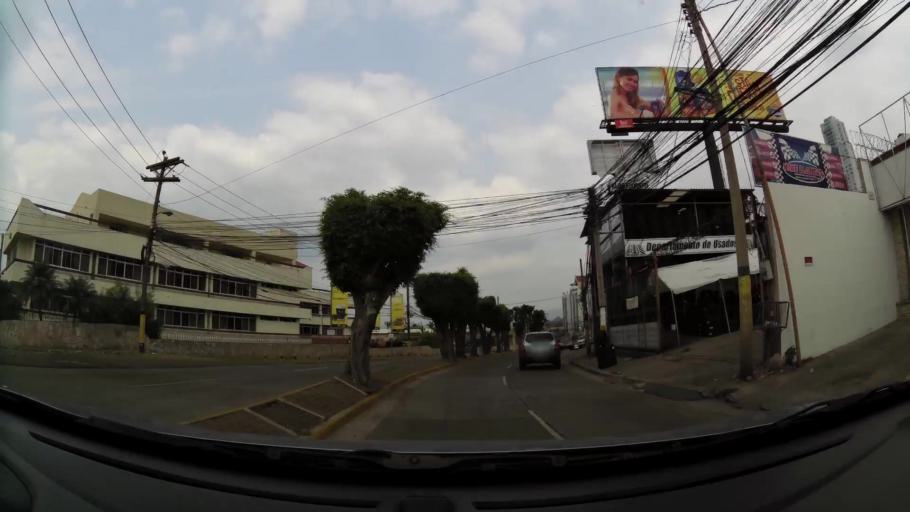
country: HN
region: Francisco Morazan
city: Tegucigalpa
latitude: 14.0892
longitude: -87.1853
